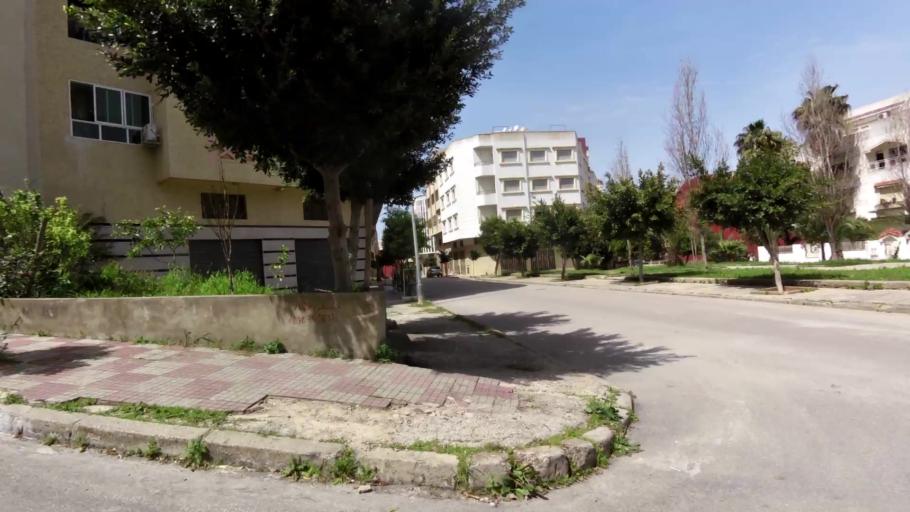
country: MA
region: Tanger-Tetouan
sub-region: Tanger-Assilah
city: Tangier
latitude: 35.7556
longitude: -5.8367
